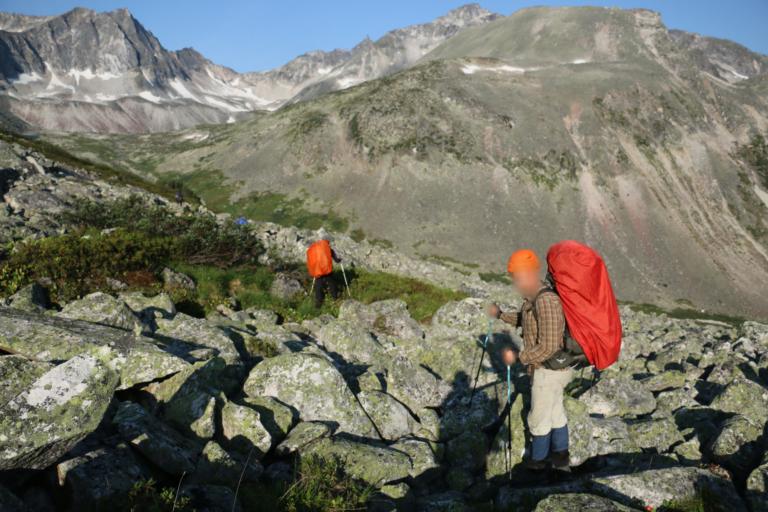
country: RU
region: Respublika Buryatiya
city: Novyy Uoyan
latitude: 56.2267
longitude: 110.9516
